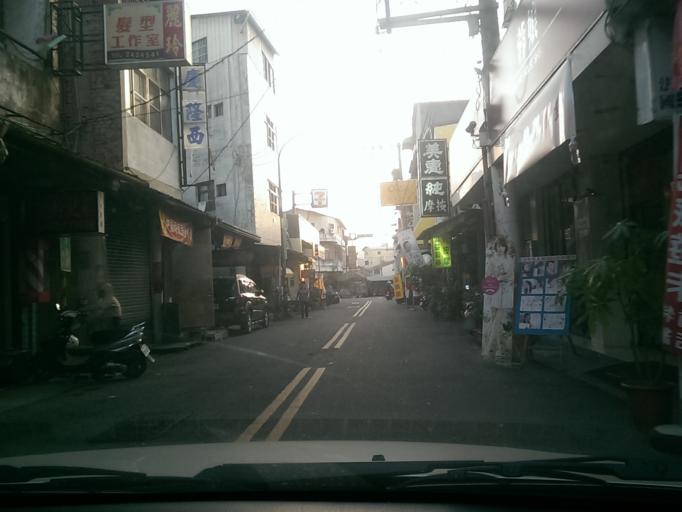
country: TW
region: Taiwan
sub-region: Nantou
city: Puli
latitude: 23.9627
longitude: 120.9665
